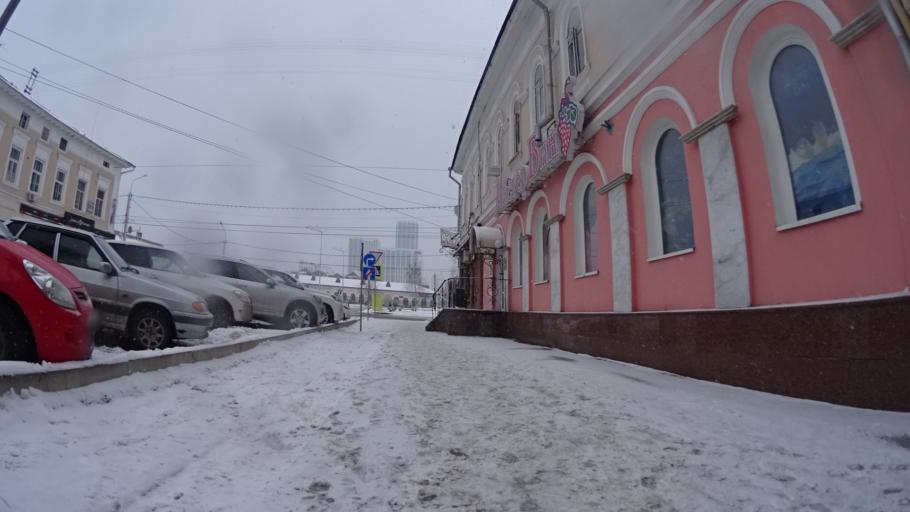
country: RU
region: Bashkortostan
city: Ufa
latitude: 54.7270
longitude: 55.9445
